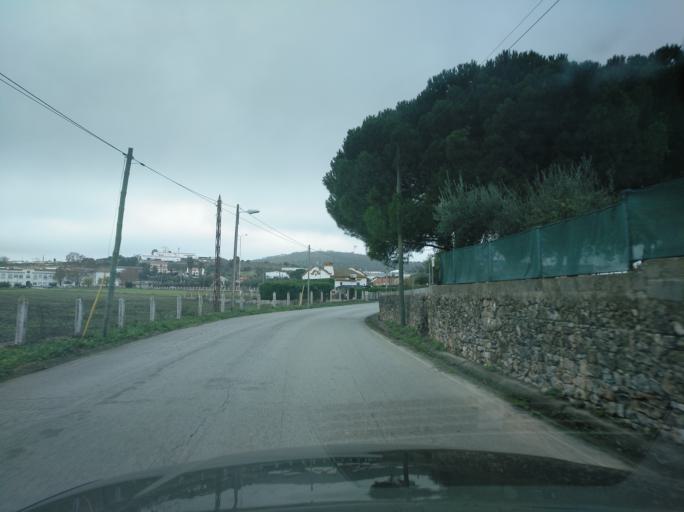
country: PT
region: Portalegre
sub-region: Elvas
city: Elvas
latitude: 38.8895
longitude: -7.1400
